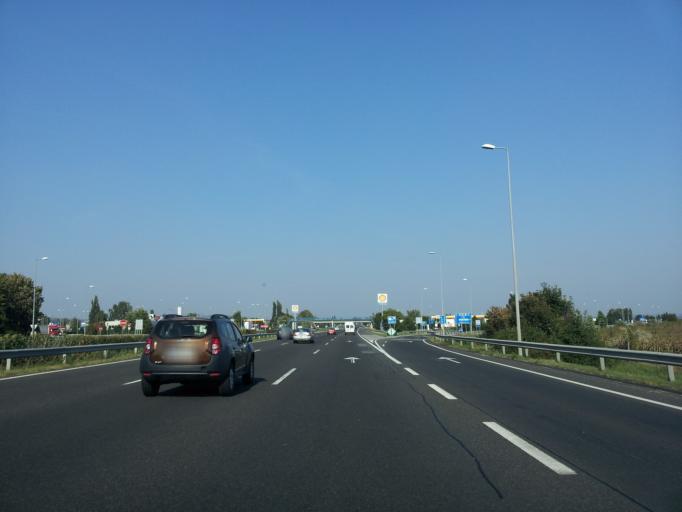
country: HU
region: Fejer
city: Szekesfehervar
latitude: 47.1751
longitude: 18.4736
